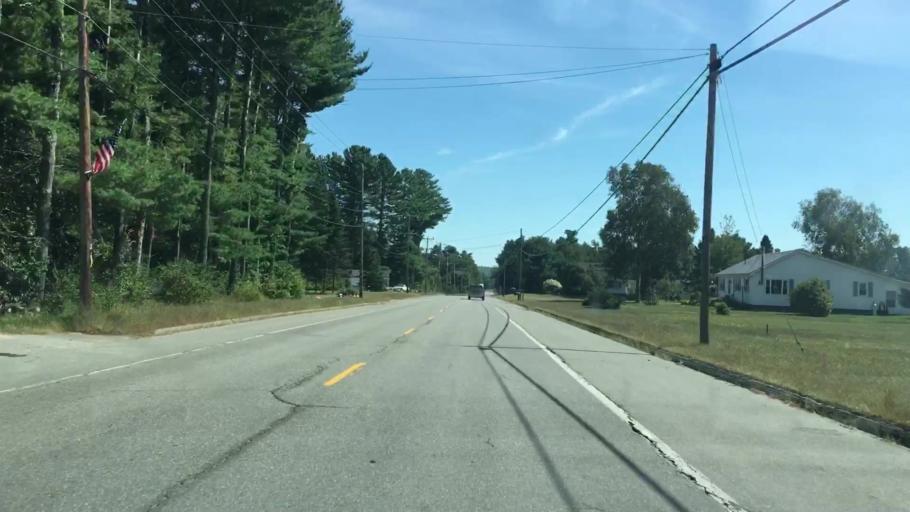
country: US
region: Maine
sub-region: Piscataquis County
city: Milo
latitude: 45.2394
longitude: -68.9676
